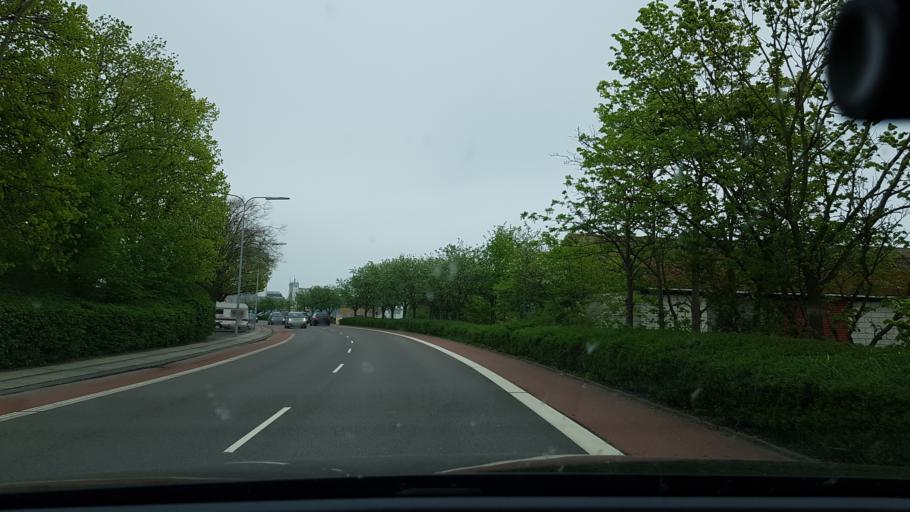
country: DK
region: Capital Region
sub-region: Bornholm Kommune
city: Nexo
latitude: 55.0591
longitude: 15.1332
